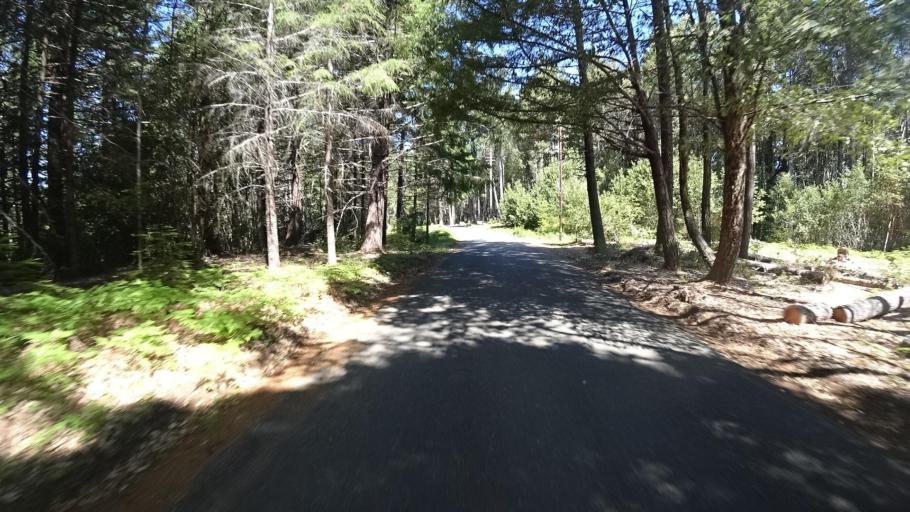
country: US
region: California
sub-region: Humboldt County
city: Redway
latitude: 40.1475
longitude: -124.0198
